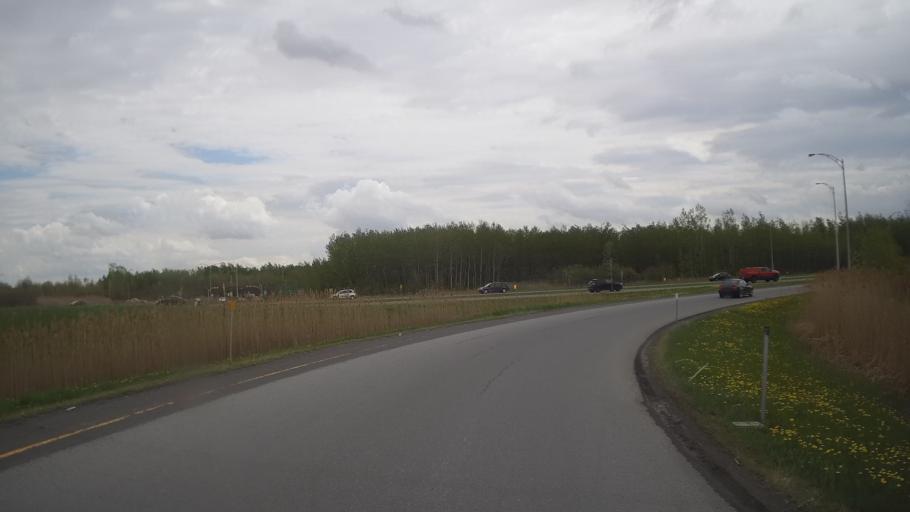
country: CA
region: Quebec
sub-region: Monteregie
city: La Prairie
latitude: 45.4022
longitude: -73.4635
